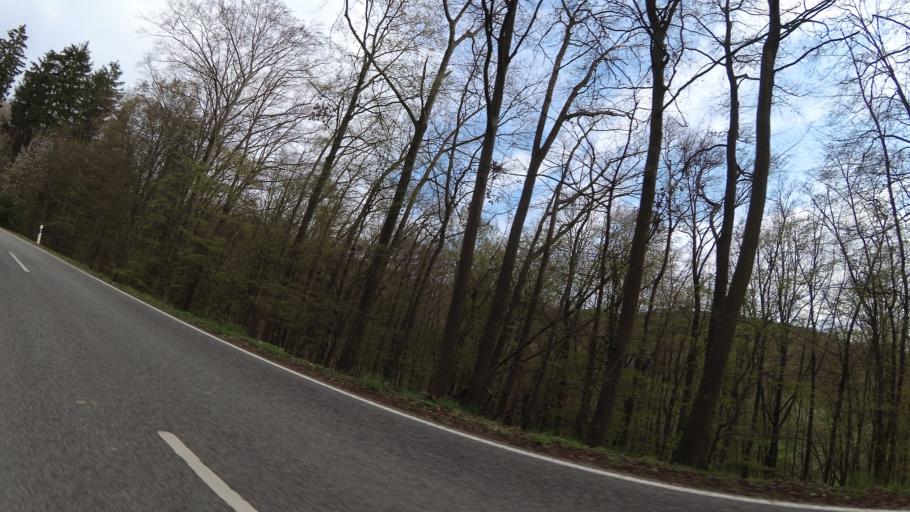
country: DE
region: Rheinland-Pfalz
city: Herschweiler-Pettersheim
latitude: 49.4838
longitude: 7.3580
